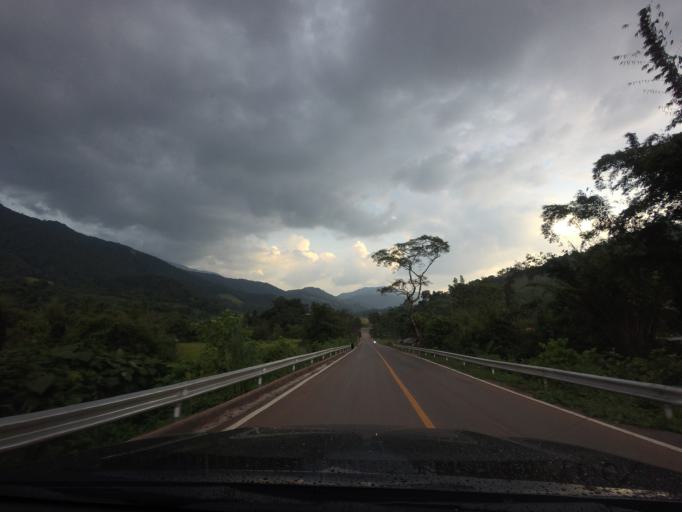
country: TH
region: Nan
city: Bo Kluea
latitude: 19.2325
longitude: 101.1822
